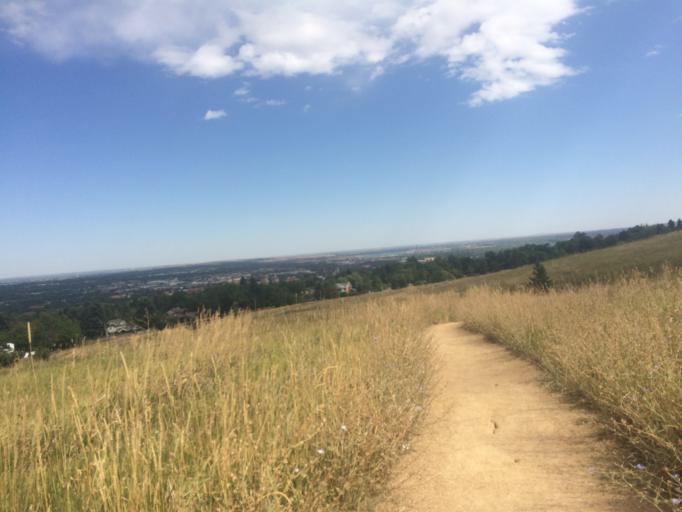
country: US
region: Colorado
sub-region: Boulder County
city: Boulder
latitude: 39.9985
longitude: -105.2871
